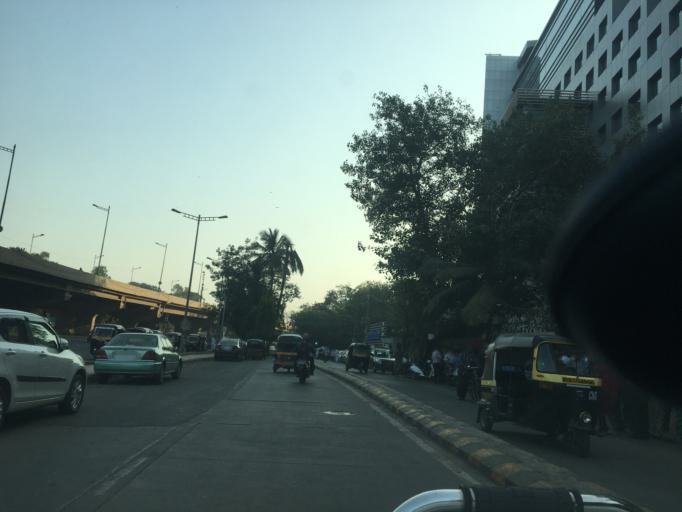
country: IN
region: Maharashtra
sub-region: Mumbai Suburban
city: Powai
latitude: 19.1463
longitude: 72.8557
